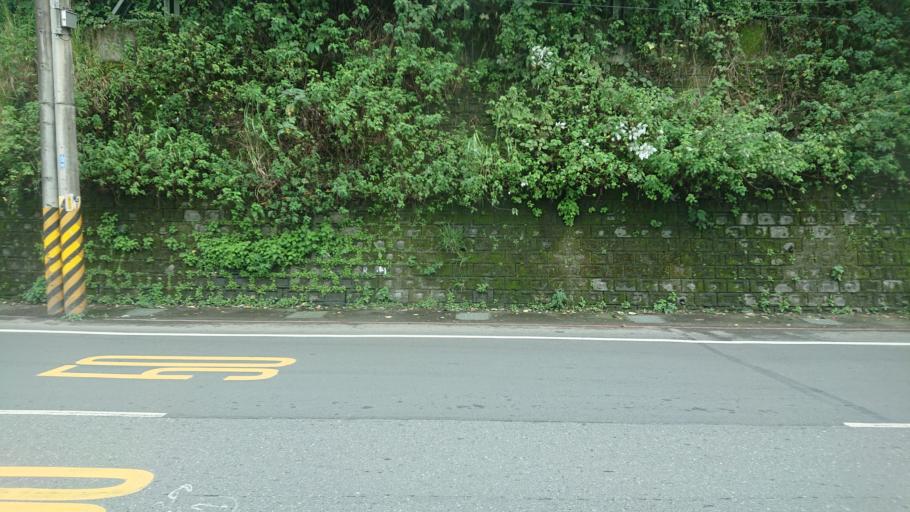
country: TW
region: Taiwan
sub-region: Taoyuan
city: Taoyuan
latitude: 24.9404
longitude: 121.3958
